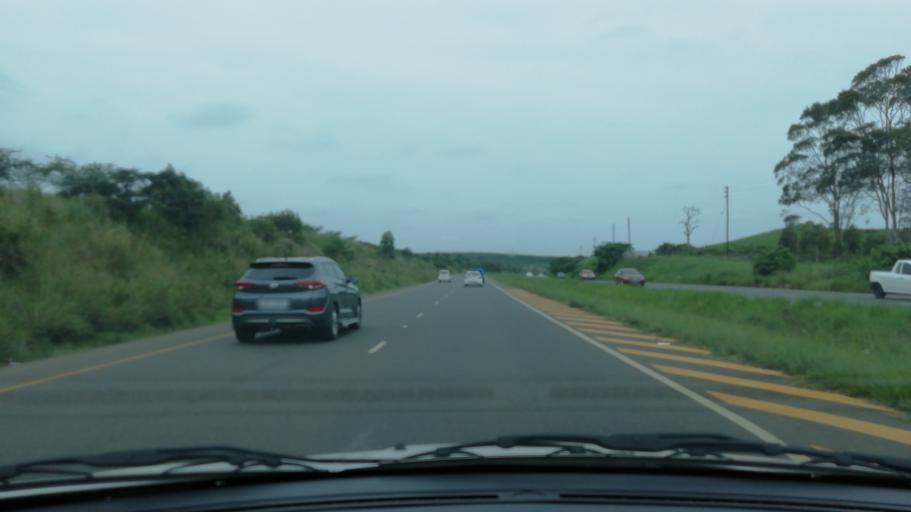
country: ZA
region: KwaZulu-Natal
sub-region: uThungulu District Municipality
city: Empangeni
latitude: -28.7668
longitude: 31.9186
